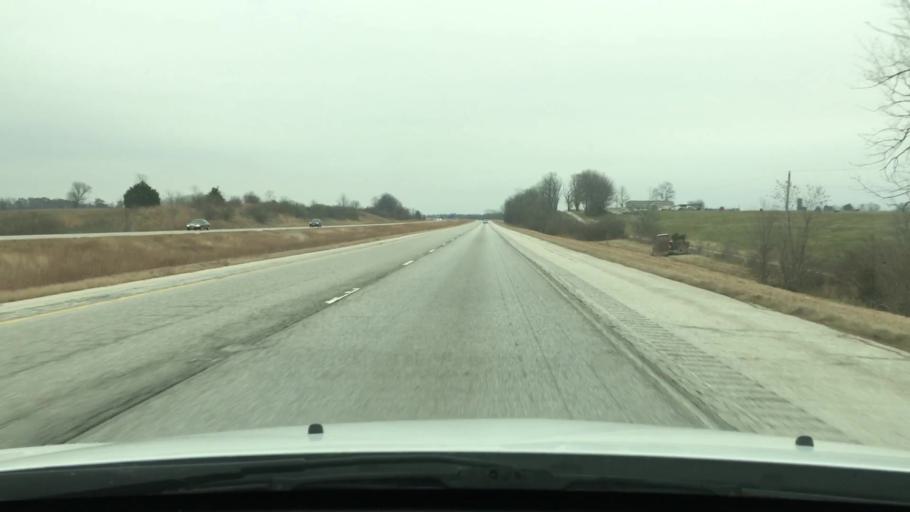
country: US
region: Illinois
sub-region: Morgan County
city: South Jacksonville
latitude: 39.6803
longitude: -90.2781
